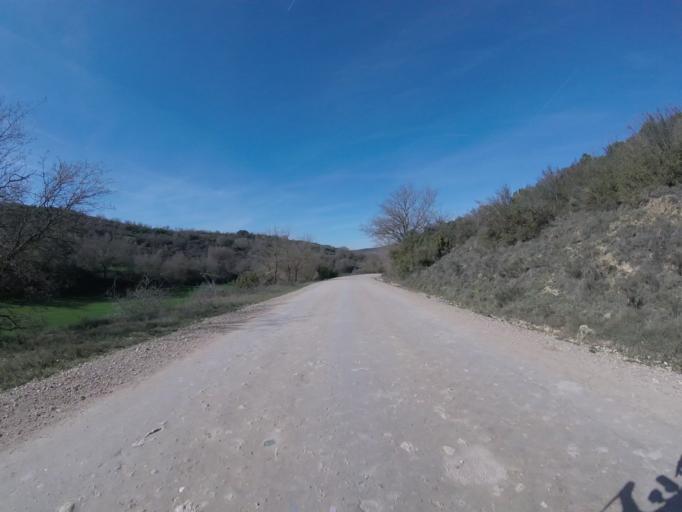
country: ES
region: Navarre
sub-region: Provincia de Navarra
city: Oteiza
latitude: 42.6460
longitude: -1.9642
